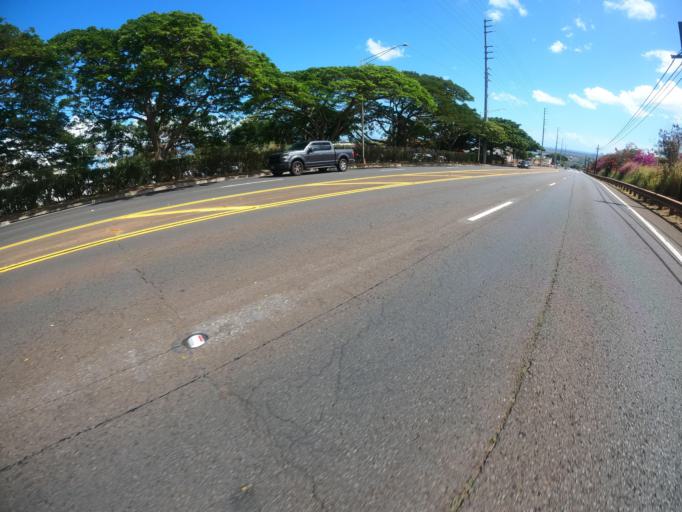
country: US
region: Hawaii
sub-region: Honolulu County
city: Village Park
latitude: 21.3906
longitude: -158.0355
